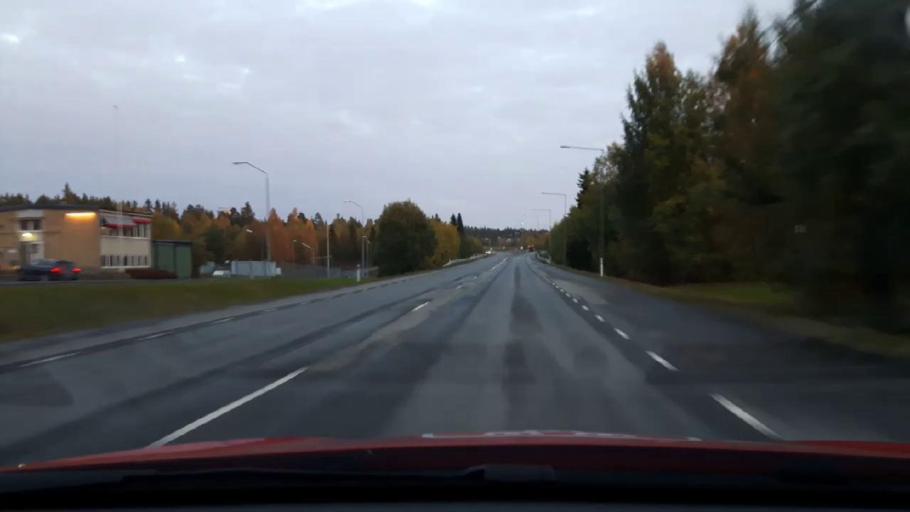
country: SE
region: Jaemtland
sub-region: OEstersunds Kommun
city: Ostersund
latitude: 63.2026
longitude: 14.6415
